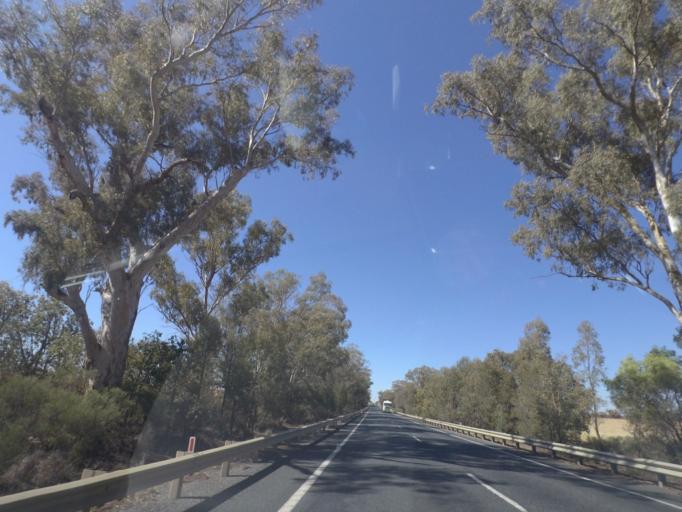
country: AU
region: New South Wales
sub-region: Bland
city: West Wyalong
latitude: -34.1737
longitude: 147.1146
